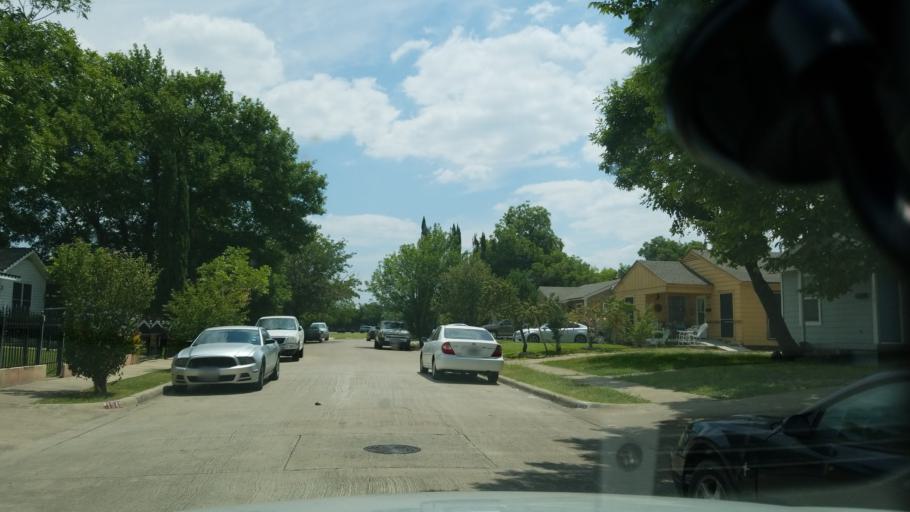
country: US
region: Texas
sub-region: Dallas County
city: Grand Prairie
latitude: 32.7496
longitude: -96.9824
